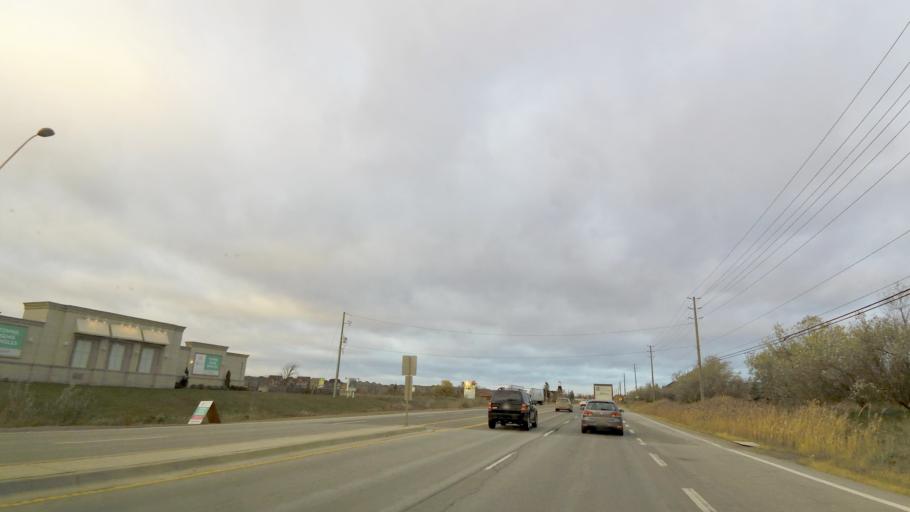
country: CA
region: Ontario
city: Oakville
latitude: 43.4664
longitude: -79.7432
